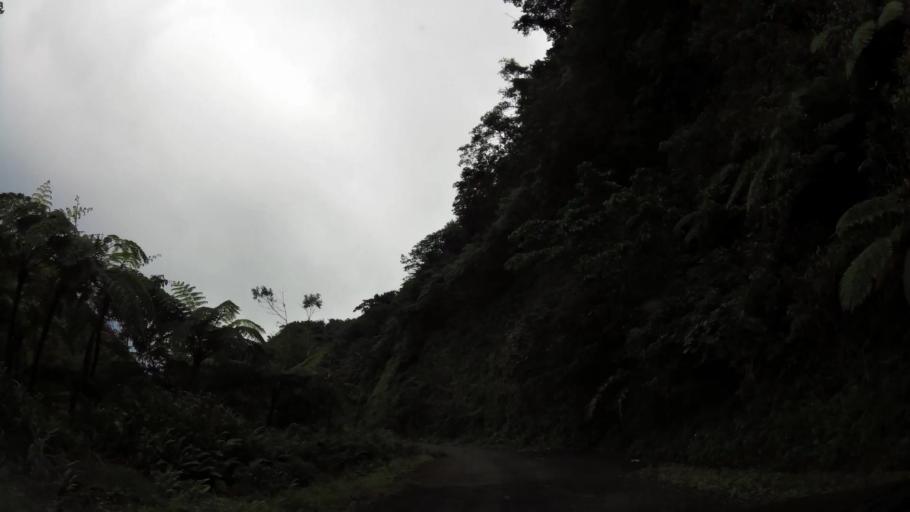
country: DM
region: Saint John
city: Portsmouth
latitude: 15.6153
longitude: -61.4438
